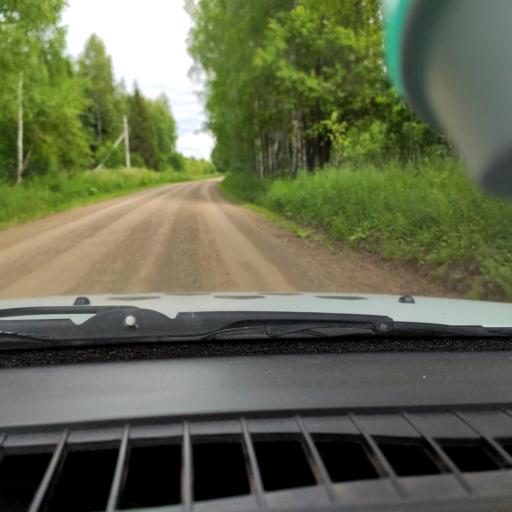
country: RU
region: Perm
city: Suksun
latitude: 57.2045
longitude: 57.6243
